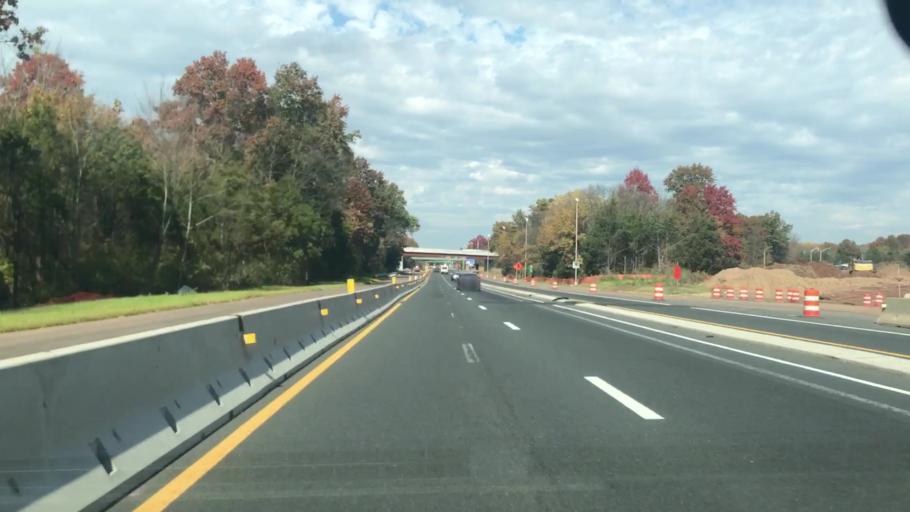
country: US
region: New Jersey
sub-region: Somerset County
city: Bridgewater
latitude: 40.6390
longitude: -74.6444
